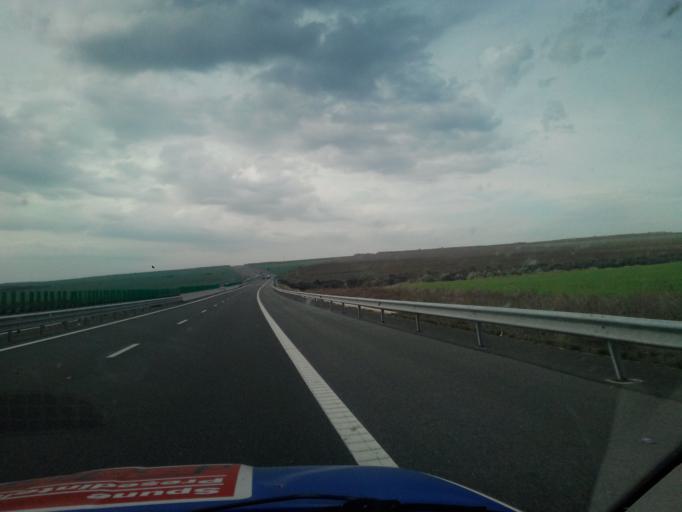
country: RO
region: Constanta
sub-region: Comuna Valu lui Traian
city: Valu lui Traian
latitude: 44.1384
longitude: 28.4442
